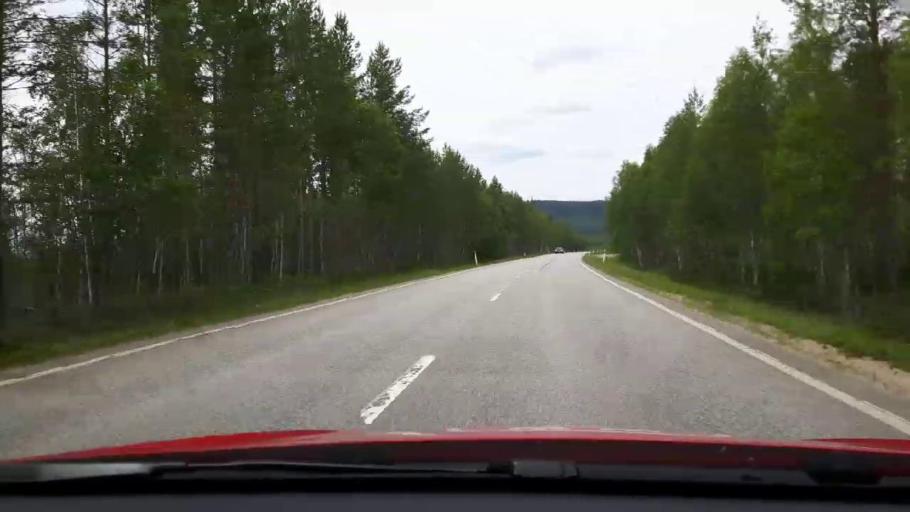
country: SE
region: Jaemtland
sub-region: Harjedalens Kommun
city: Sveg
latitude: 62.0830
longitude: 14.2547
